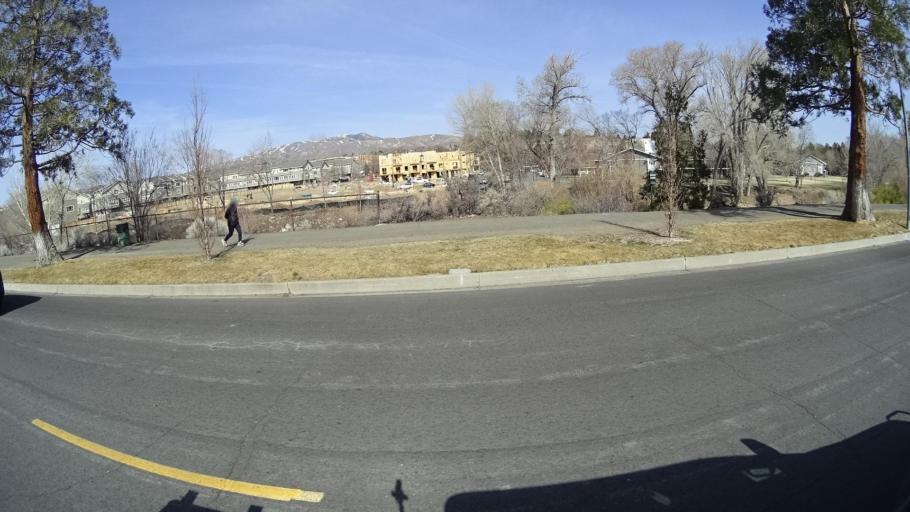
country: US
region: Nevada
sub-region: Washoe County
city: Reno
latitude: 39.5178
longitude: -119.8408
